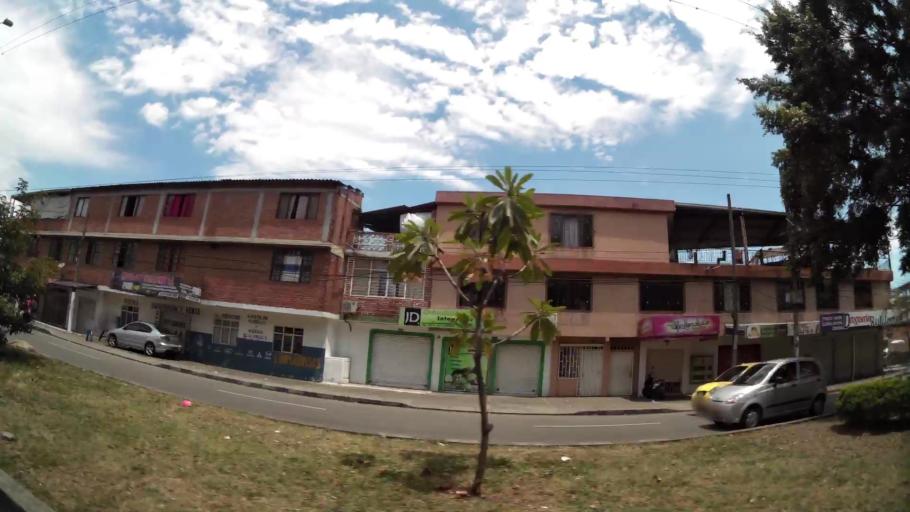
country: CO
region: Valle del Cauca
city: Cali
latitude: 3.4456
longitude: -76.5033
